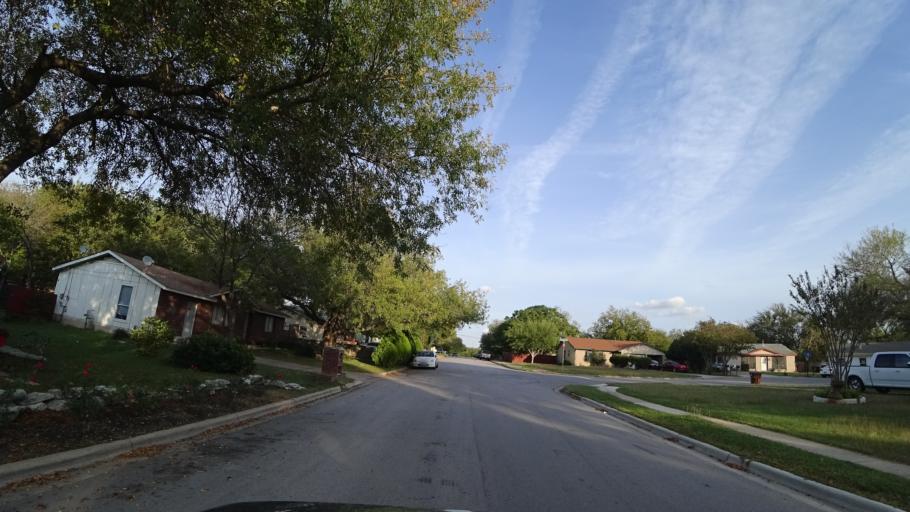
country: US
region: Texas
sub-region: Williamson County
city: Round Rock
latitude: 30.4986
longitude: -97.6684
